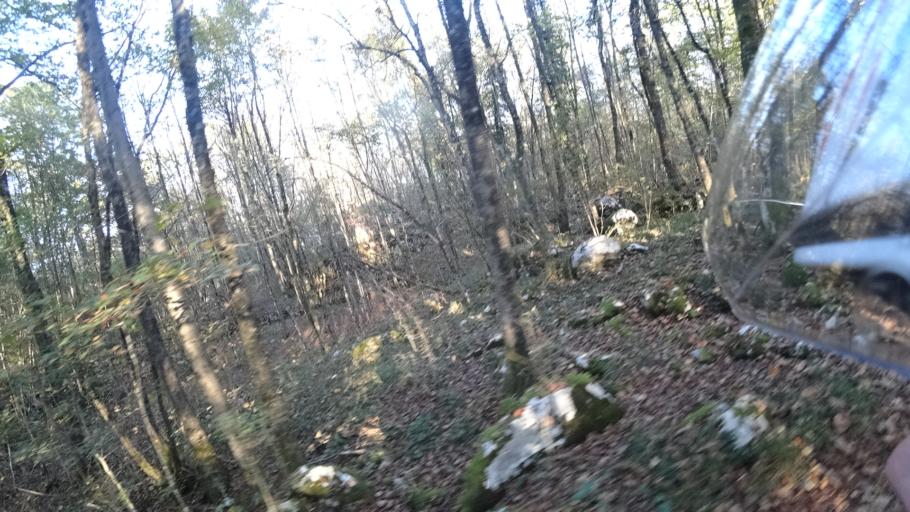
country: HR
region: Primorsko-Goranska
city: Matulji
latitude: 45.4015
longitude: 14.3145
